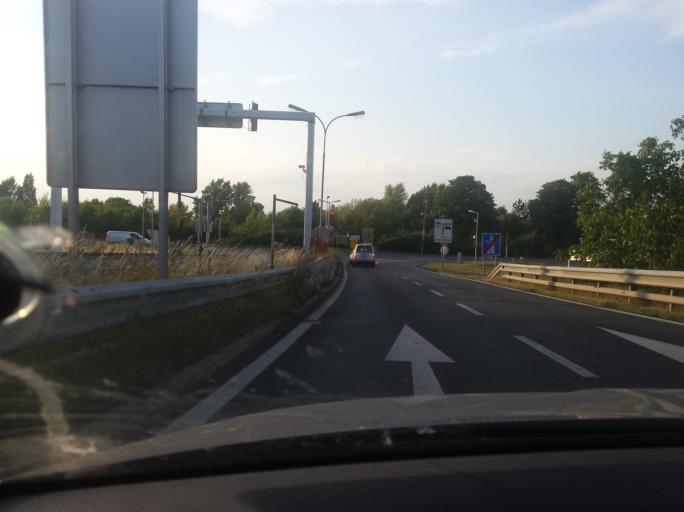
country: AT
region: Lower Austria
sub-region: Politischer Bezirk Wien-Umgebung
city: Schwechat
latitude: 48.1475
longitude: 16.4859
